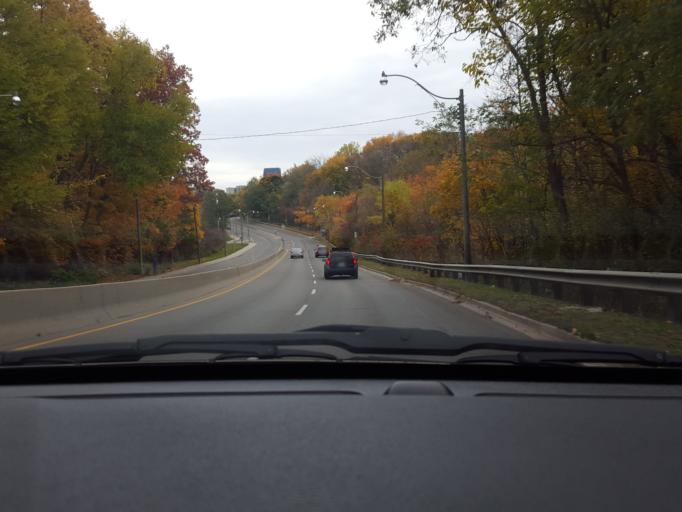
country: CA
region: Ontario
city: Toronto
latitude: 43.6824
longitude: -79.3833
